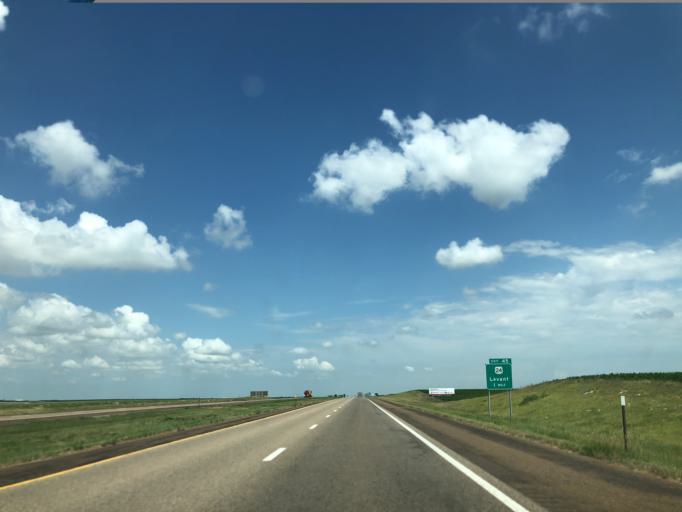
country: US
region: Kansas
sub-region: Thomas County
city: Colby
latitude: 39.3660
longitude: -101.2267
